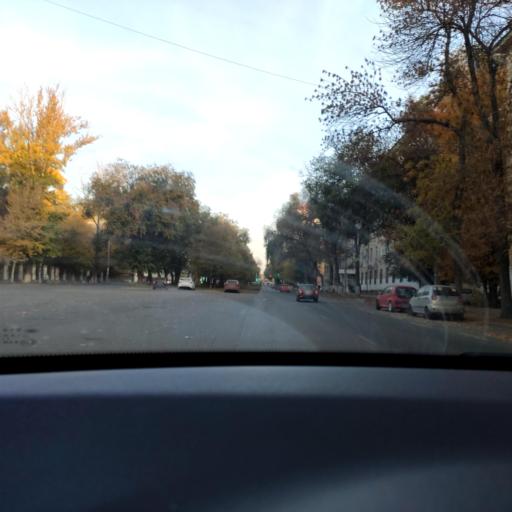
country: RU
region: Samara
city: Samara
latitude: 53.2137
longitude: 50.2475
